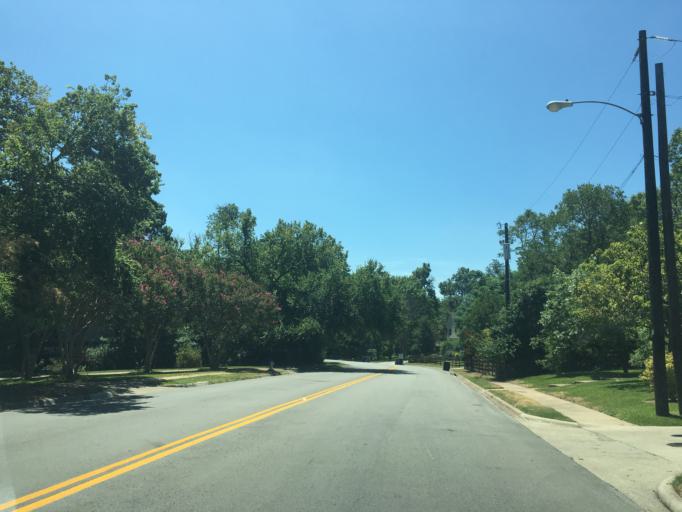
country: US
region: Texas
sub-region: Dallas County
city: Highland Park
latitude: 32.8476
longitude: -96.7099
